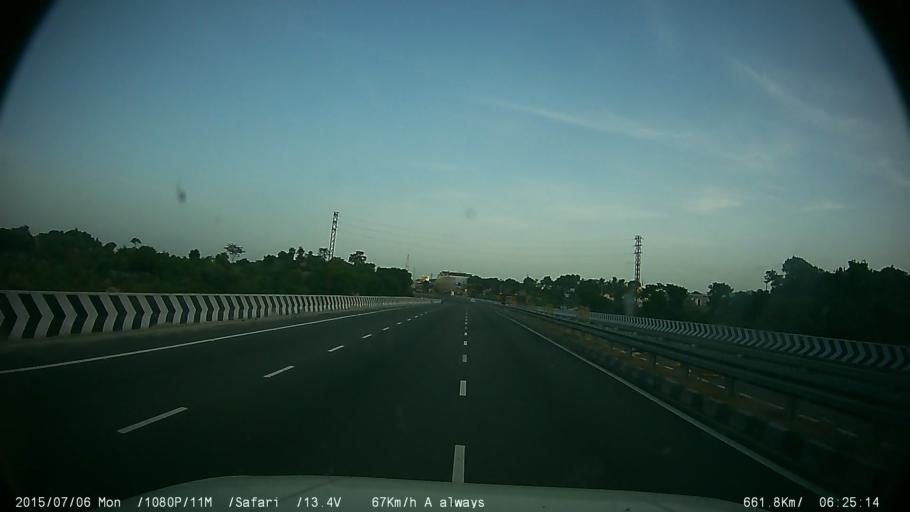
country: IN
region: Tamil Nadu
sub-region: Krishnagiri
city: Kelamangalam
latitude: 12.6604
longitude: 78.0171
